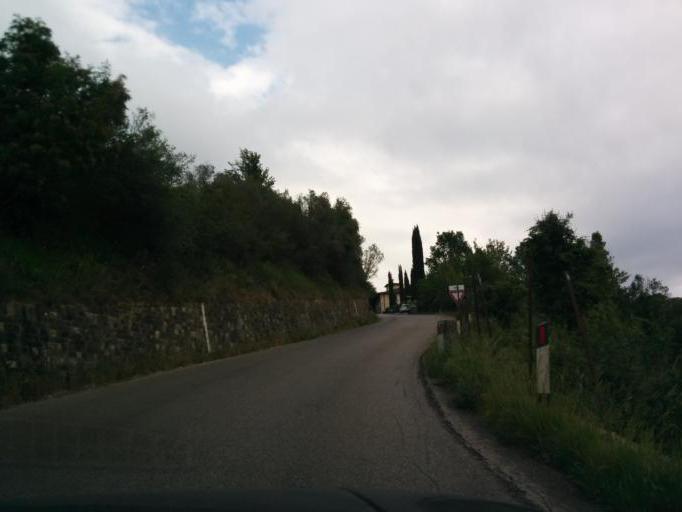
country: IT
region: Tuscany
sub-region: Province of Florence
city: San Casciano in Val di Pesa
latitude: 43.6432
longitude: 11.1730
